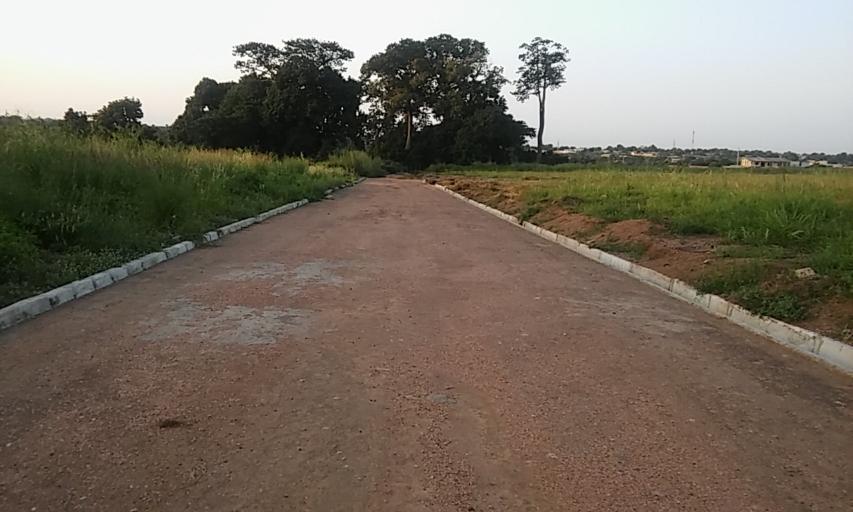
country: CI
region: Vallee du Bandama
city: Bouake
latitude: 7.6891
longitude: -5.0649
